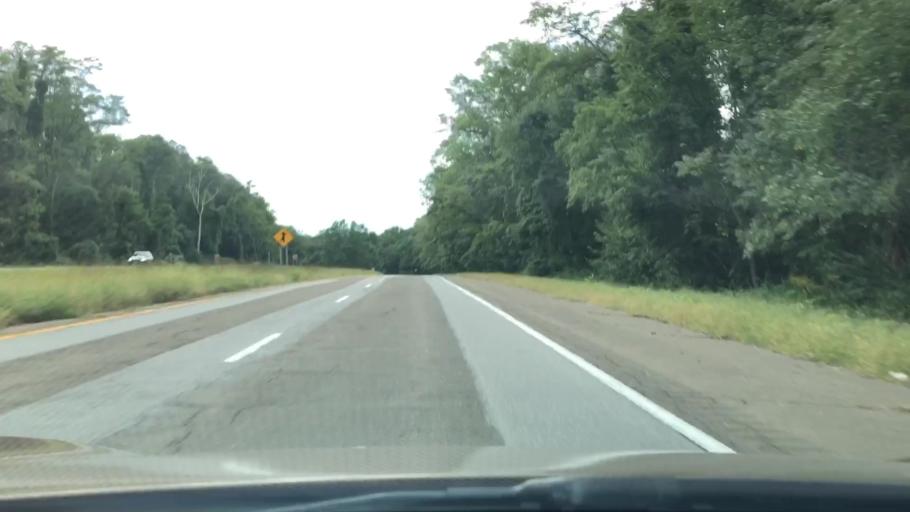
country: US
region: New York
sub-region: Westchester County
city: Briarcliff Manor
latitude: 41.1136
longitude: -73.8352
